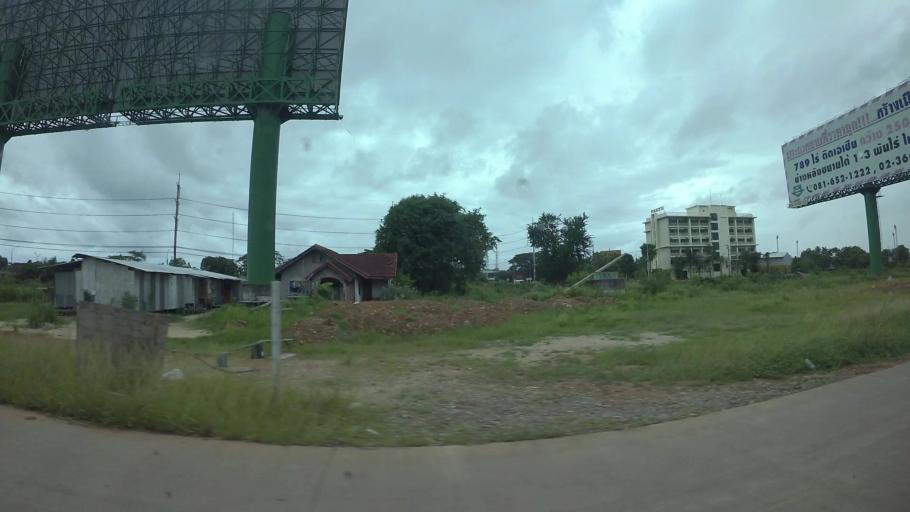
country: TH
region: Chon Buri
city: Si Racha
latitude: 13.2085
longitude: 100.9454
